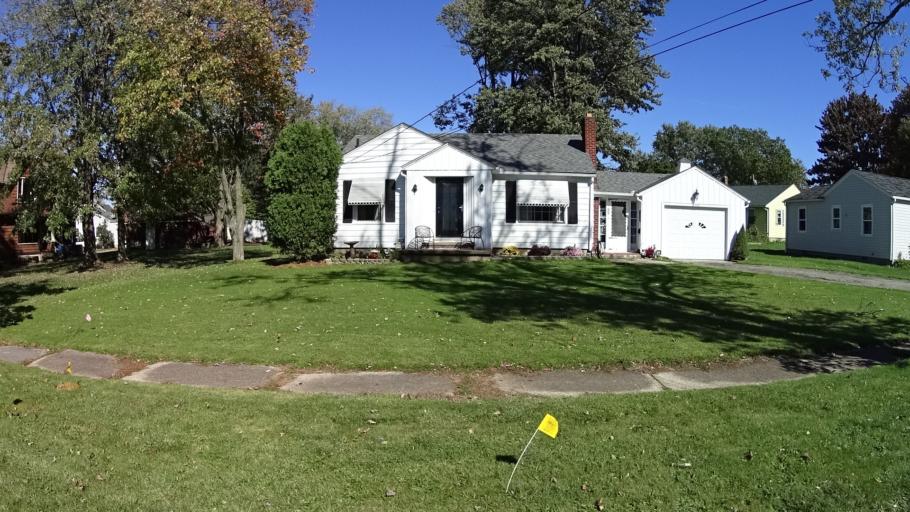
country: US
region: Ohio
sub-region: Lorain County
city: Amherst
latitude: 41.3897
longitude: -82.2177
